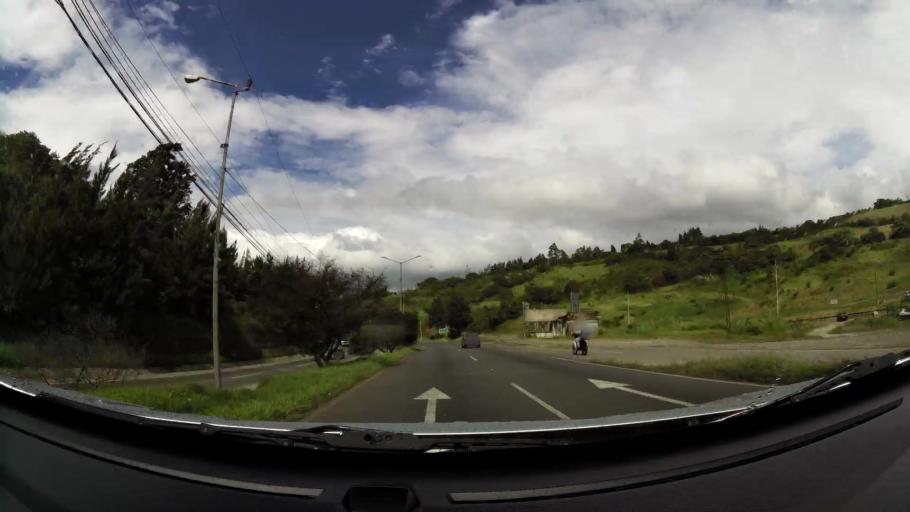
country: CR
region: Cartago
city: Tres Rios
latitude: 9.9001
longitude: -83.9462
